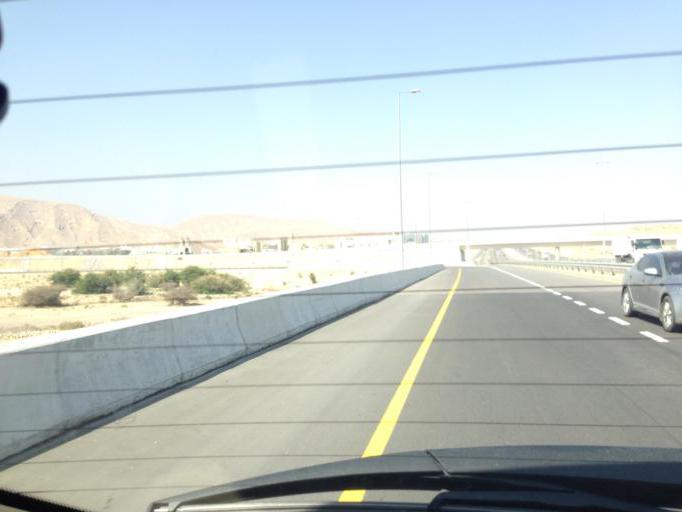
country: OM
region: Muhafazat Masqat
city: As Sib al Jadidah
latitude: 23.5665
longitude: 58.1890
